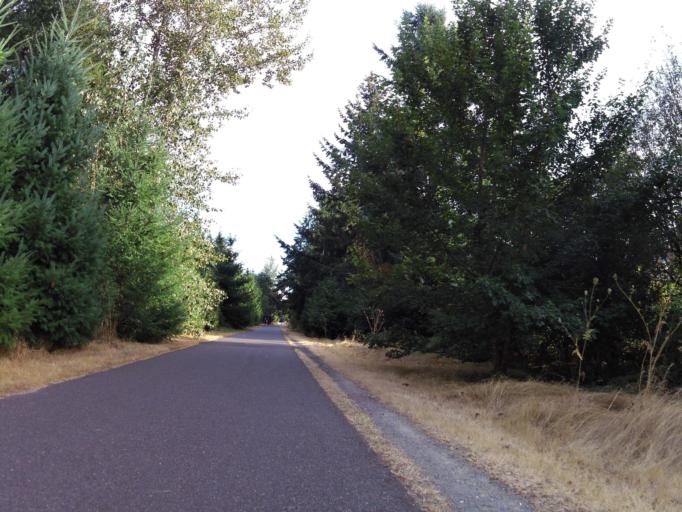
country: US
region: Washington
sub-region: Thurston County
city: Lacey
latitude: 46.9859
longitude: -122.8274
